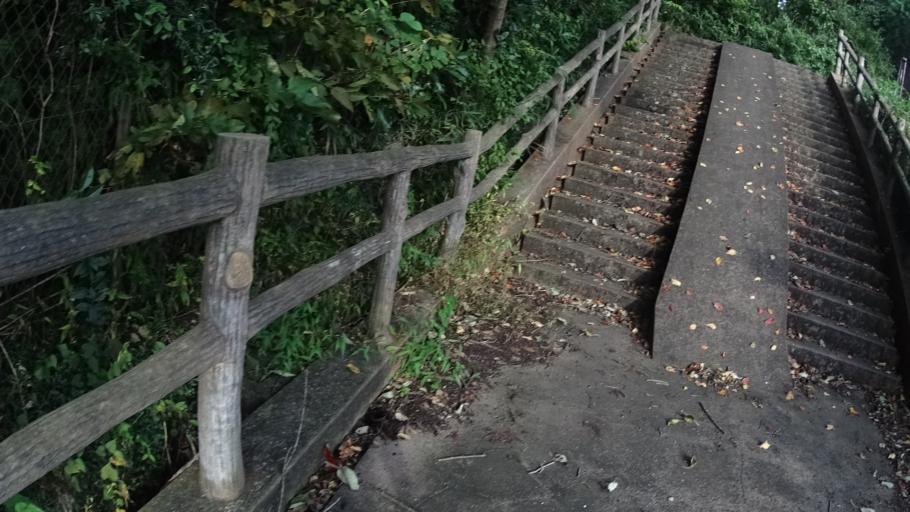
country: JP
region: Kanagawa
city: Zushi
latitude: 35.3554
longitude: 139.6017
